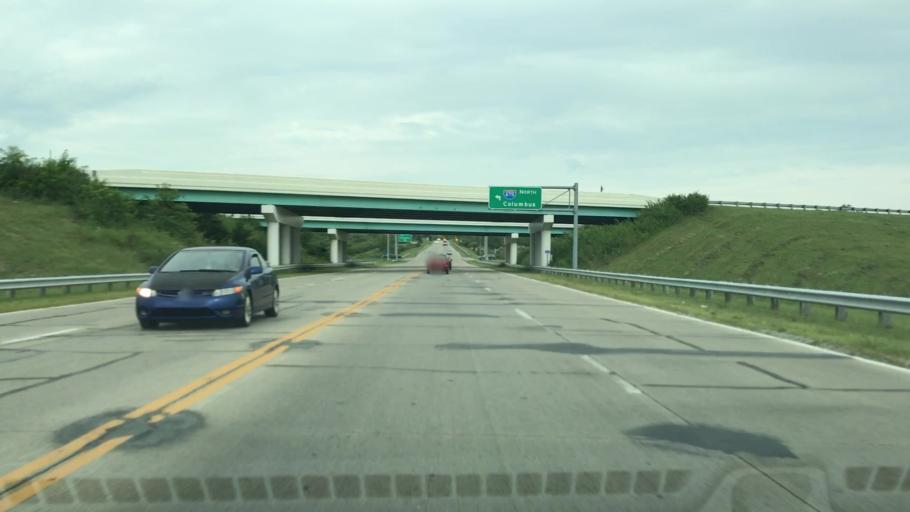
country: US
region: Ohio
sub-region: Greene County
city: Fairborn
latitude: 39.8168
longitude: -84.0015
